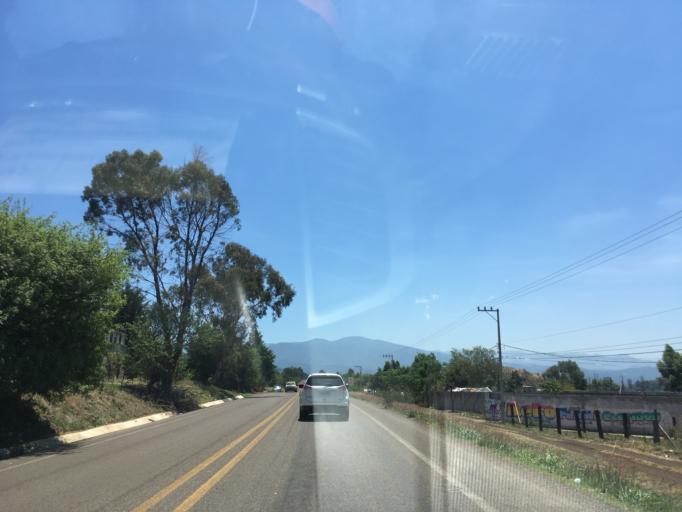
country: MX
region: Michoacan
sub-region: Zitacuaro
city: Puentecillas (Tercera Manzana de Zirahuato)
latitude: 19.4796
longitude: -100.4288
